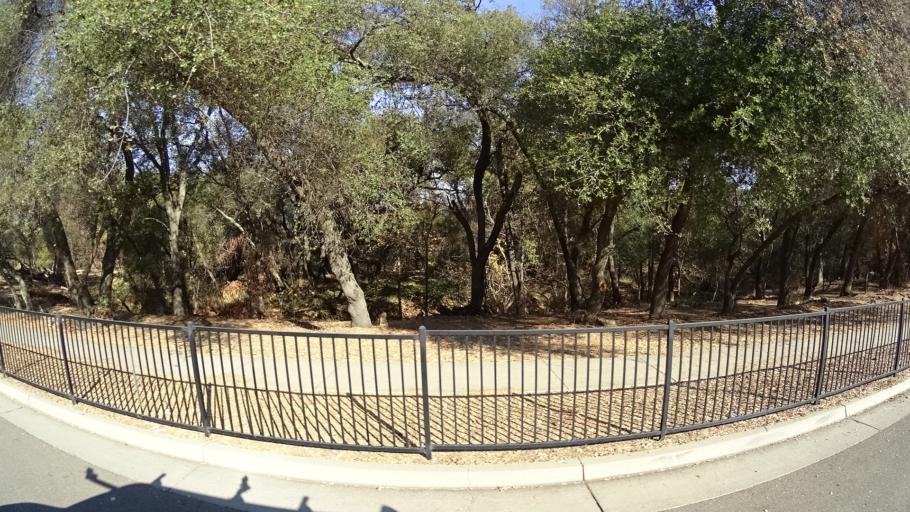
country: US
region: California
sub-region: Sacramento County
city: Citrus Heights
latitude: 38.6874
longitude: -121.2934
